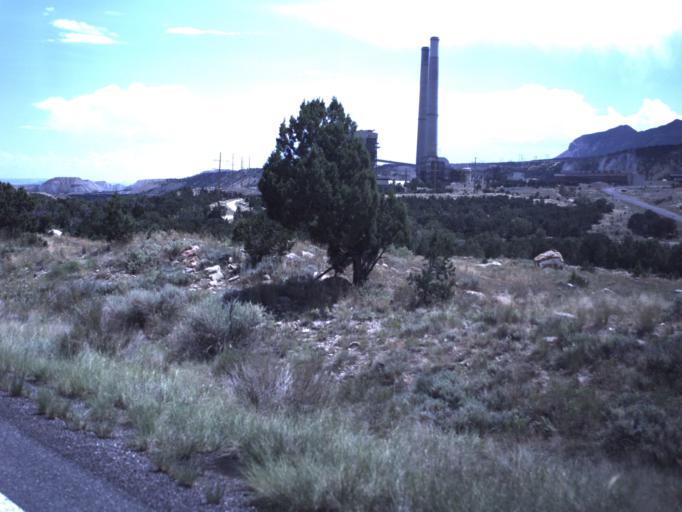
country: US
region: Utah
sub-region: Emery County
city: Huntington
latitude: 39.3880
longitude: -111.0851
